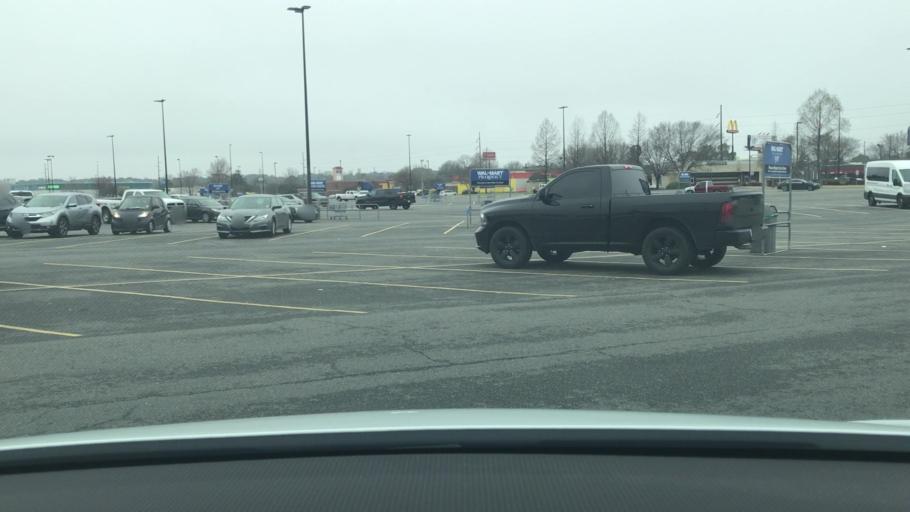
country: US
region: Louisiana
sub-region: Bossier Parish
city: Bossier City
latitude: 32.4297
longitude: -93.7120
